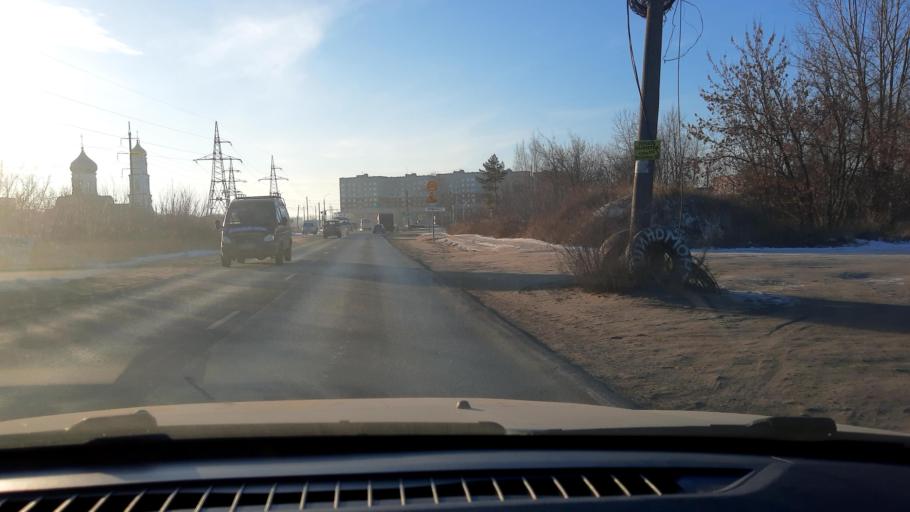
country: RU
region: Nizjnij Novgorod
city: Dzerzhinsk
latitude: 56.2482
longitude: 43.4207
